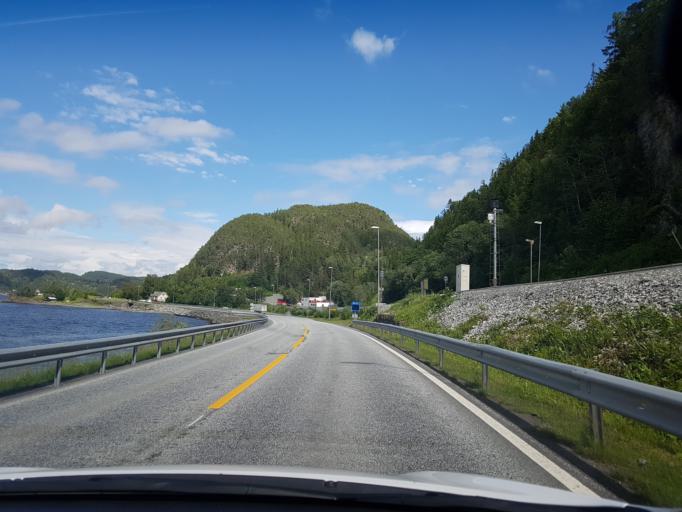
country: NO
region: Nord-Trondelag
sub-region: Stjordal
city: Stjordal
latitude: 63.5455
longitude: 10.8968
